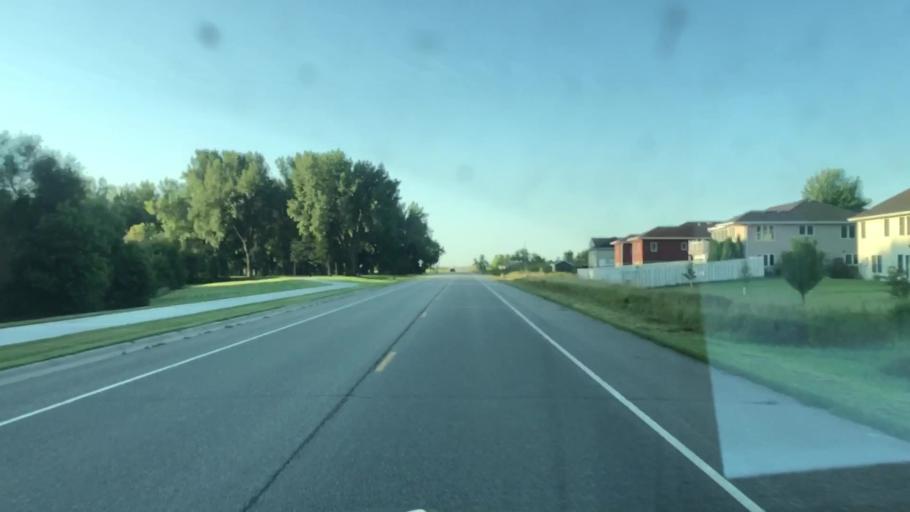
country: US
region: Minnesota
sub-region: Nobles County
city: Worthington
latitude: 43.6116
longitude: -95.6367
